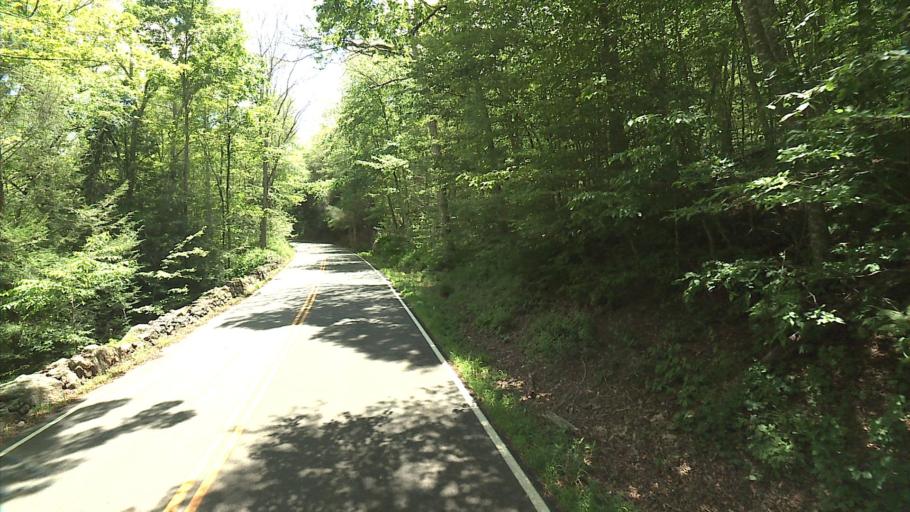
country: US
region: Connecticut
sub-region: New London County
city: Colchester
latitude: 41.4820
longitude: -72.3428
